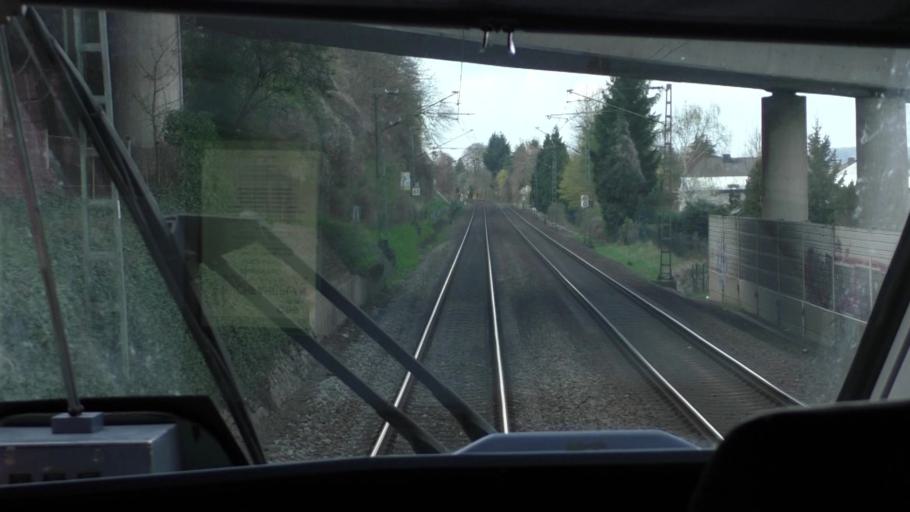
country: DE
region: Rheinland-Pfalz
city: Bad Breisig
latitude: 50.5131
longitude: 7.2925
